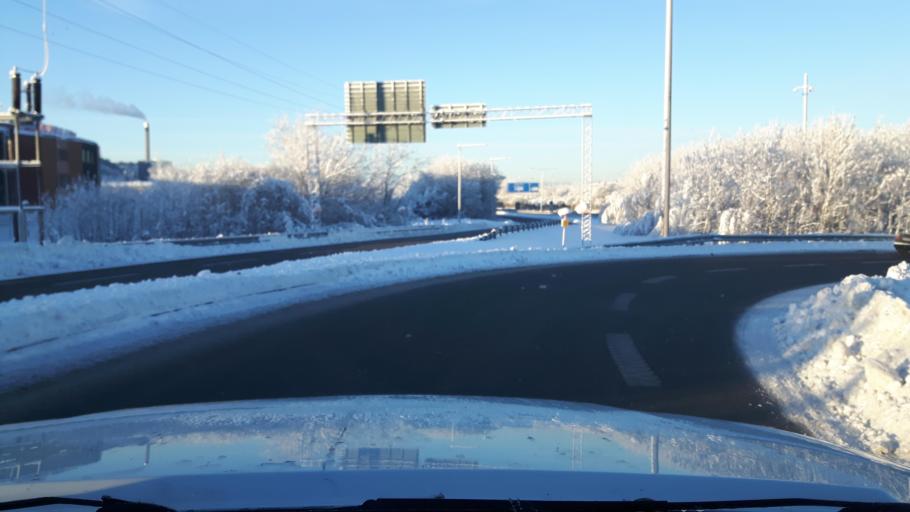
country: SE
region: Vaestra Goetaland
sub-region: Molndal
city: Moelndal
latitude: 57.6448
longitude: 12.0165
